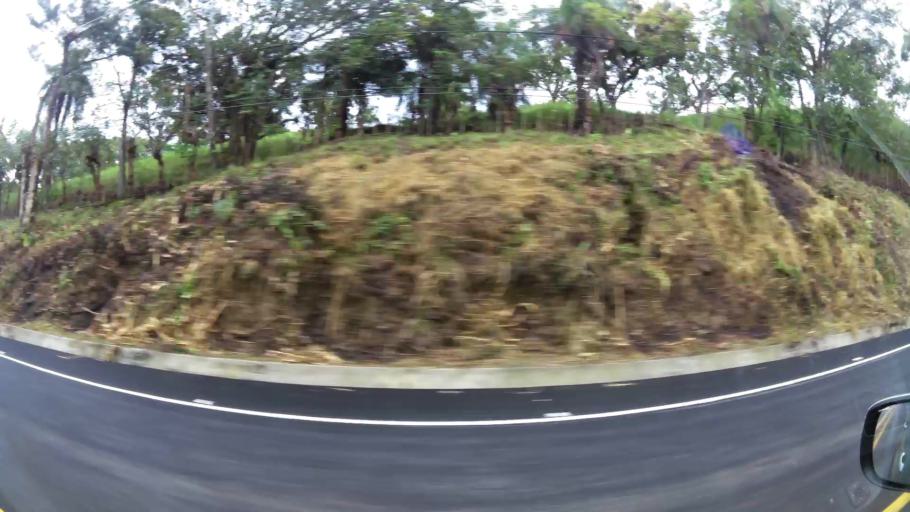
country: CR
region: Alajuela
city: Orotina
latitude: 9.9527
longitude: -84.5691
